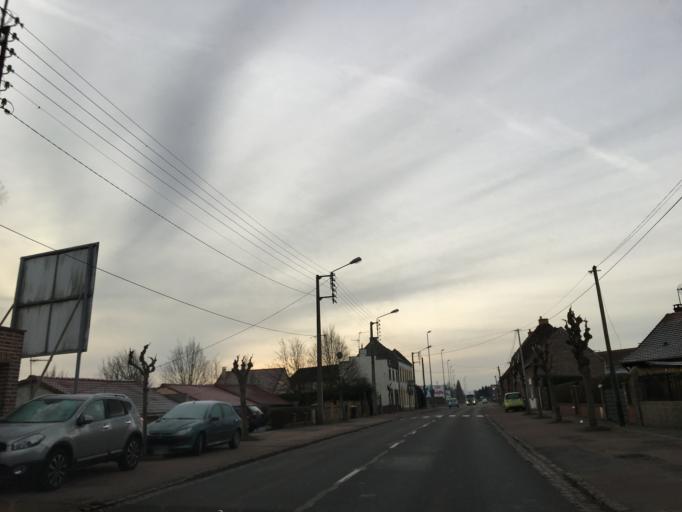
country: FR
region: Nord-Pas-de-Calais
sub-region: Departement du Pas-de-Calais
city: Courrieres
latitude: 50.4488
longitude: 2.9440
